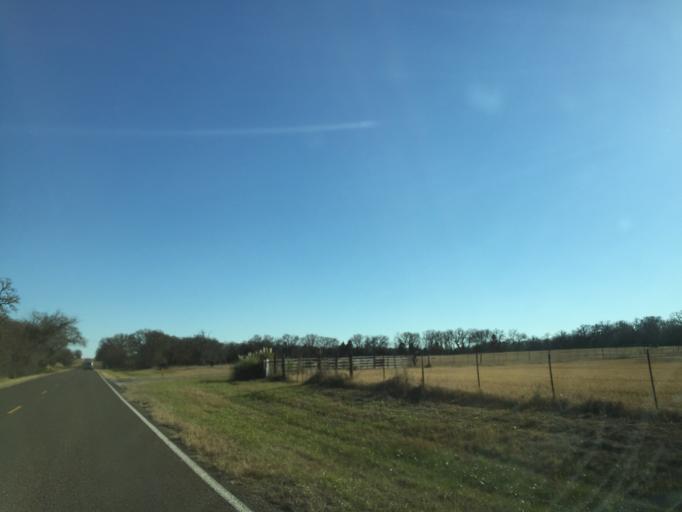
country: US
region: Texas
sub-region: Bastrop County
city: Elgin
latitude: 30.4218
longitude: -97.2584
